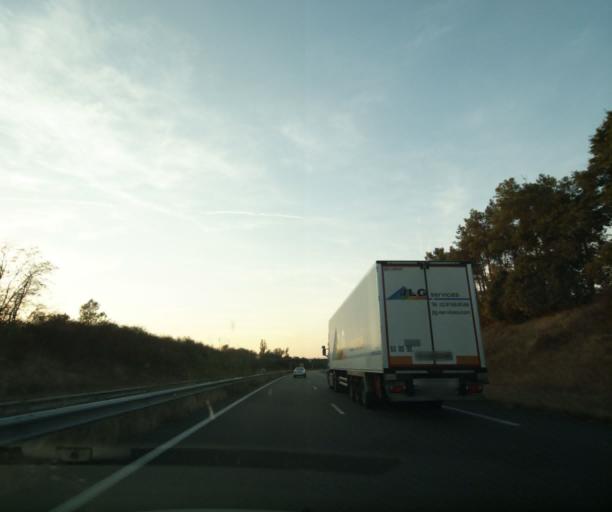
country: FR
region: Aquitaine
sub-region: Departement du Lot-et-Garonne
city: Fourques-sur-Garonne
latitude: 44.4528
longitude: 0.0887
